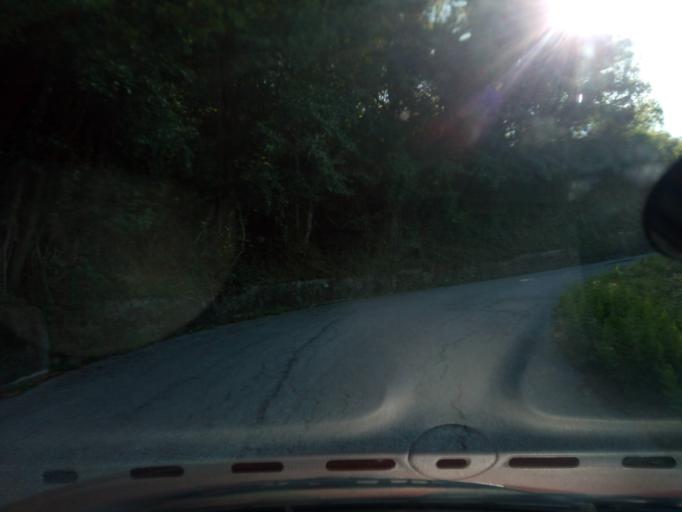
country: IT
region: Liguria
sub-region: Provincia di Genova
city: Isoverde
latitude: 44.4921
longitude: 8.8469
